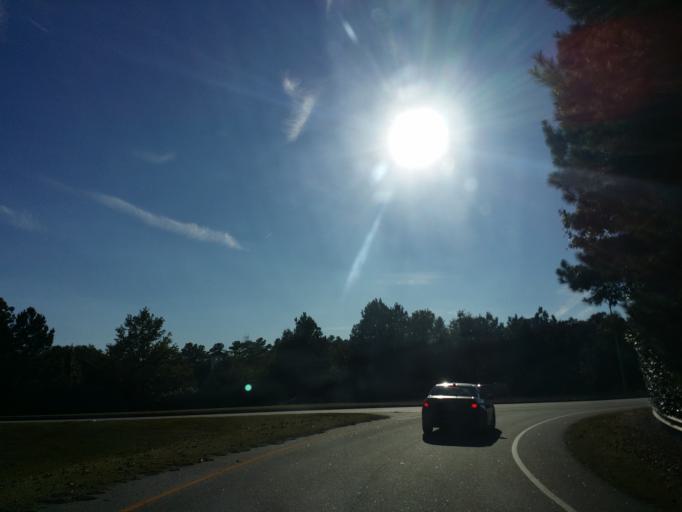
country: US
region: North Carolina
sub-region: Wake County
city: Raleigh
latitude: 35.7701
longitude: -78.6461
